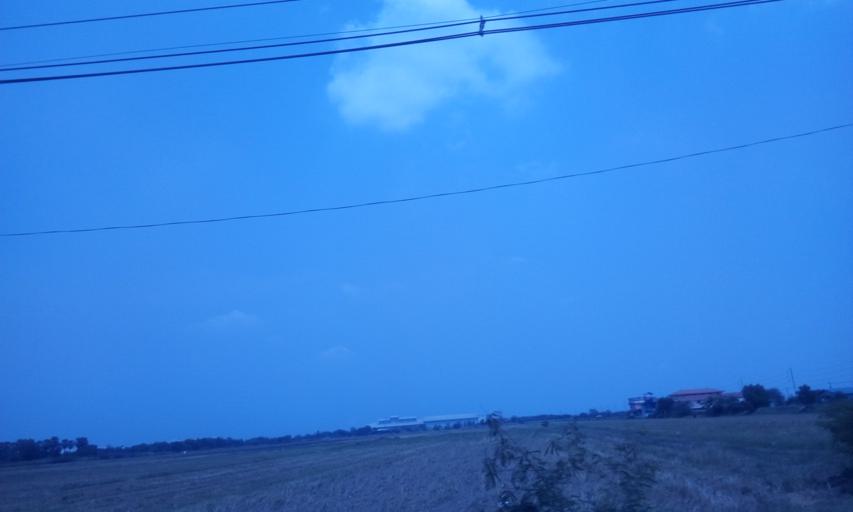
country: TH
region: Bangkok
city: Nong Chok
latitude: 13.9645
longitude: 100.9174
